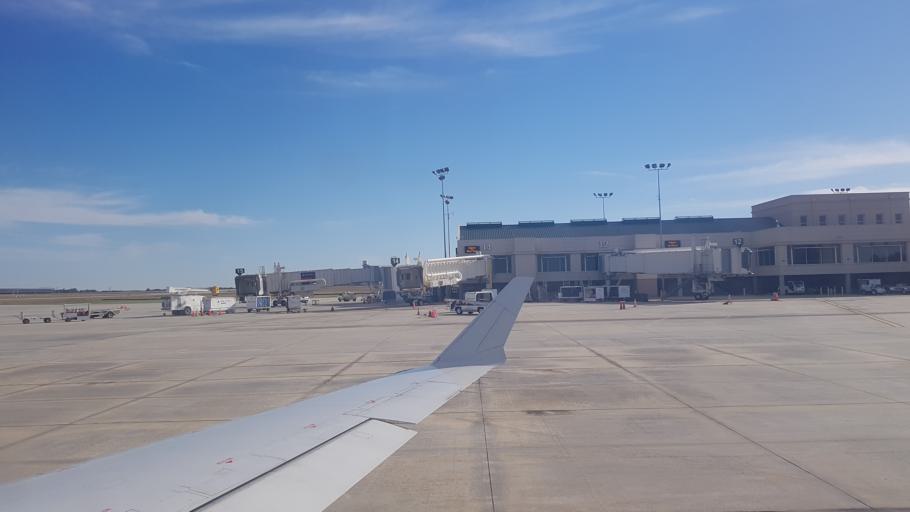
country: US
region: Georgia
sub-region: Chatham County
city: Port Wentworth
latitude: 32.1366
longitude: -81.2064
